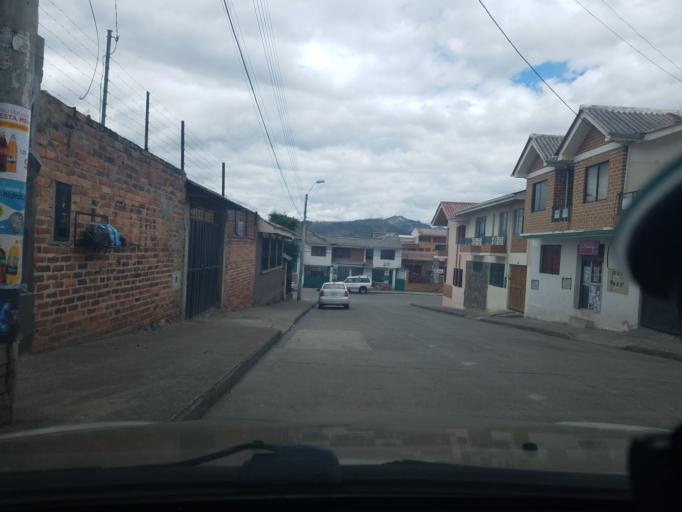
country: EC
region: Azuay
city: Cuenca
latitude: -2.8884
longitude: -78.9958
